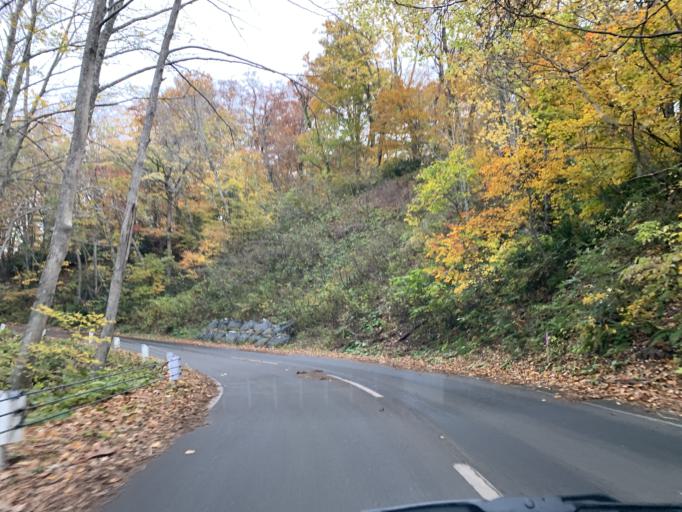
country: JP
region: Iwate
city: Mizusawa
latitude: 39.1066
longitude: 140.8621
